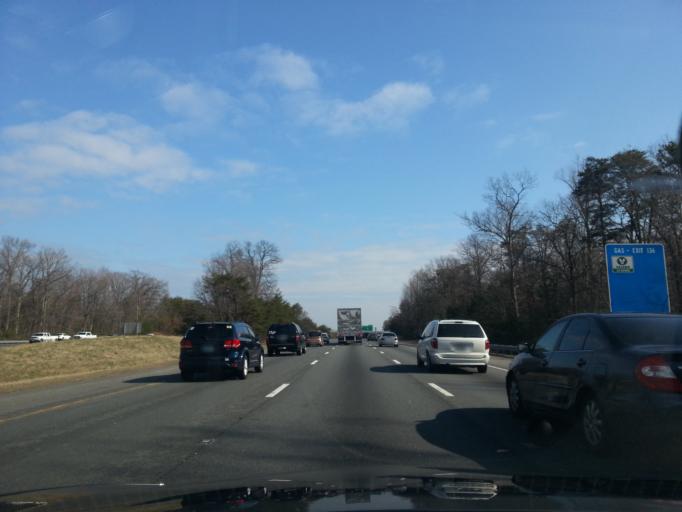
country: US
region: Virginia
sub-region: Stafford County
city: Falmouth
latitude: 38.3652
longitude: -77.4681
